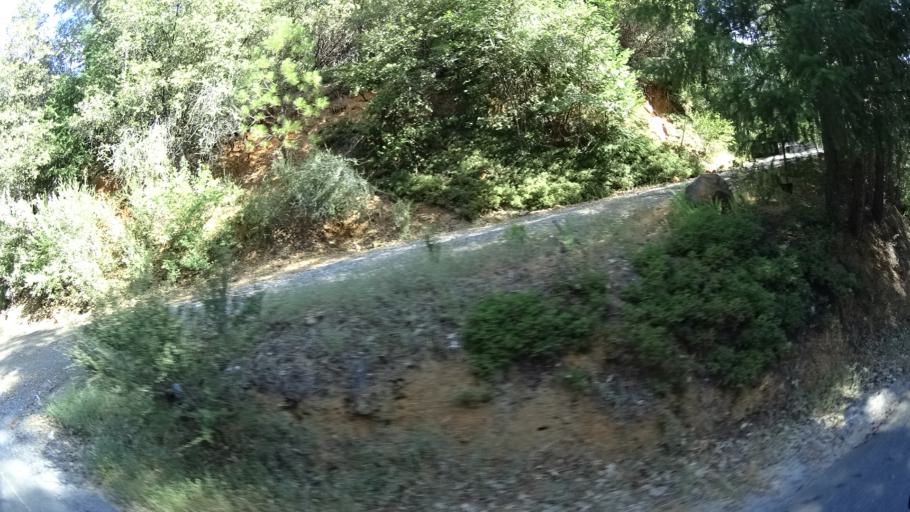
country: US
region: California
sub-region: Amador County
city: Pioneer
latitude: 38.3696
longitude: -120.4570
